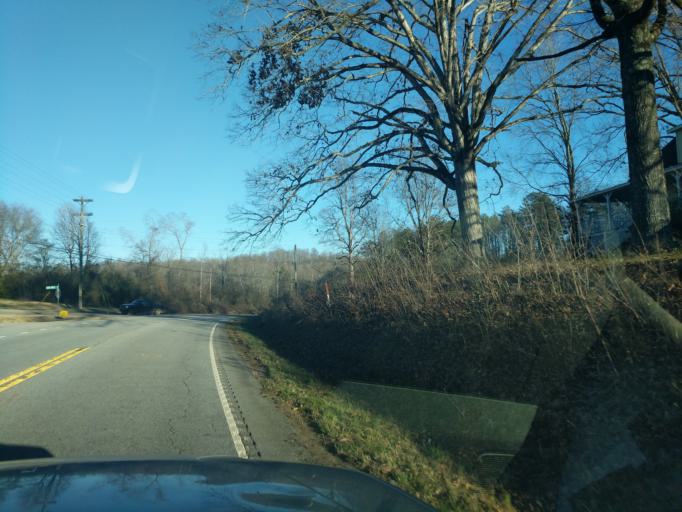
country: US
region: South Carolina
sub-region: Oconee County
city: Westminster
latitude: 34.6875
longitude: -83.1468
